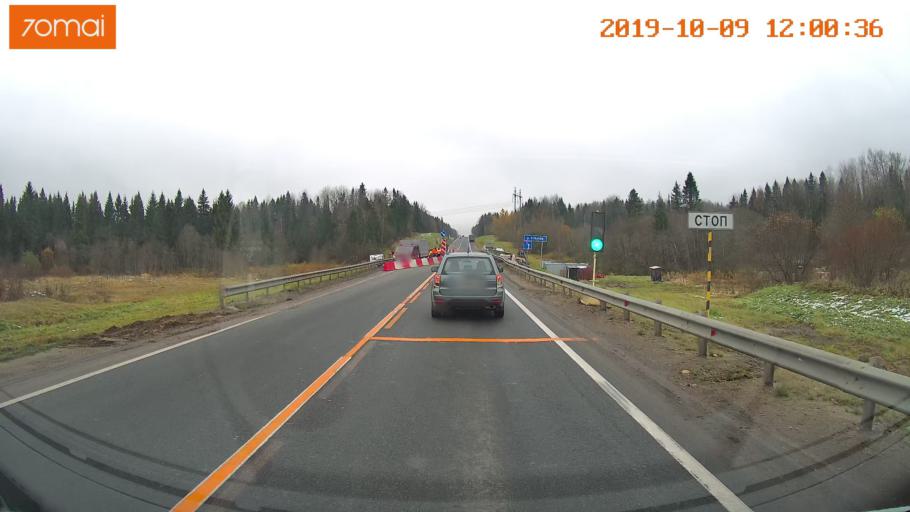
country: RU
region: Vologda
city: Gryazovets
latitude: 58.6954
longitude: 40.3002
